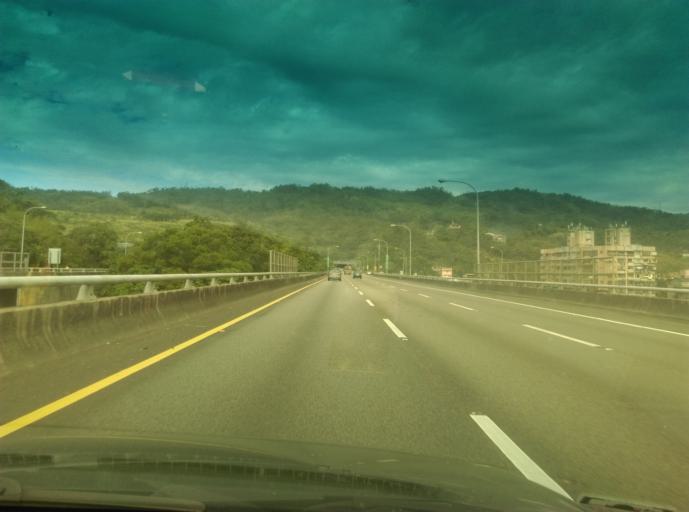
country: TW
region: Taipei
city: Taipei
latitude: 25.0029
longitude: 121.5953
